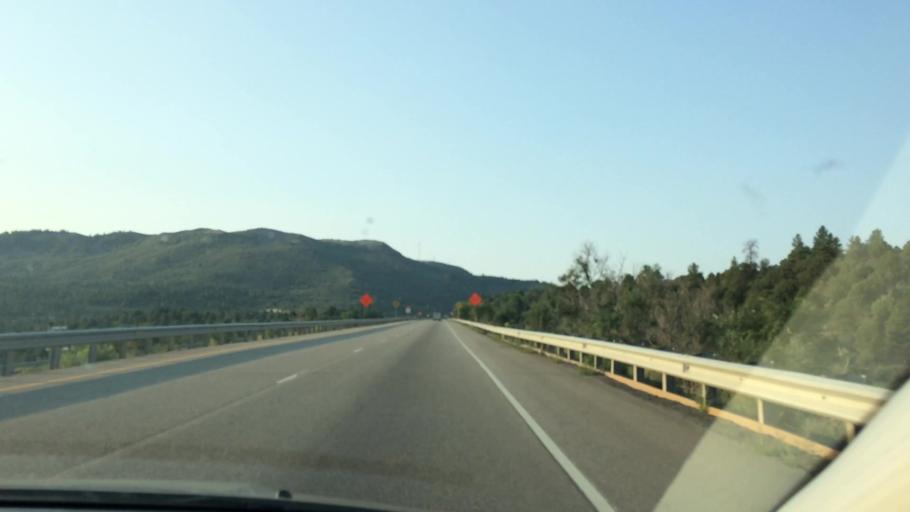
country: US
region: New Mexico
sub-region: Colfax County
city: Raton
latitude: 37.0152
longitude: -104.4827
